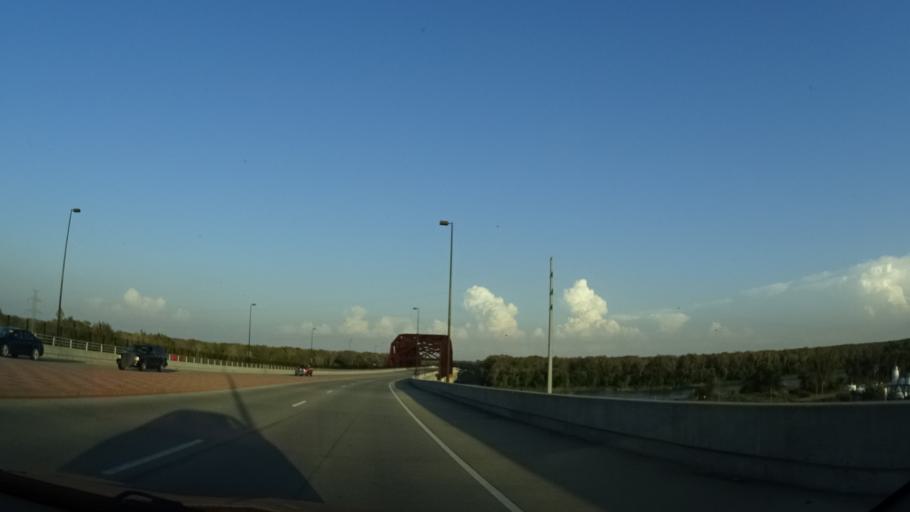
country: US
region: Nebraska
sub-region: Douglas County
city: Omaha
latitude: 41.2126
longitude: -95.9310
